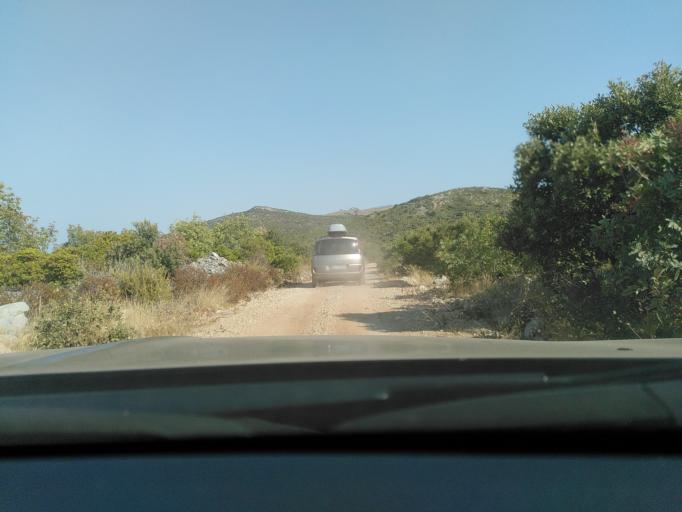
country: HR
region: Splitsko-Dalmatinska
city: Stari Grad
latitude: 43.1622
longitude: 16.5531
